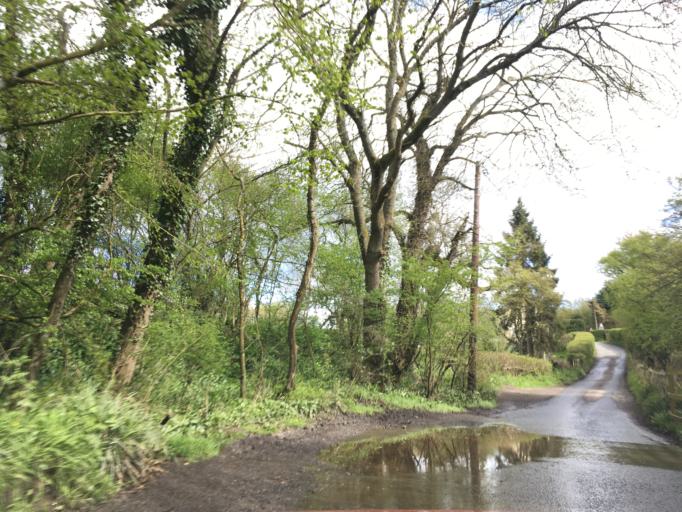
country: GB
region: England
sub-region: South Gloucestershire
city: Wickwar
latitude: 51.5980
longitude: -2.3757
